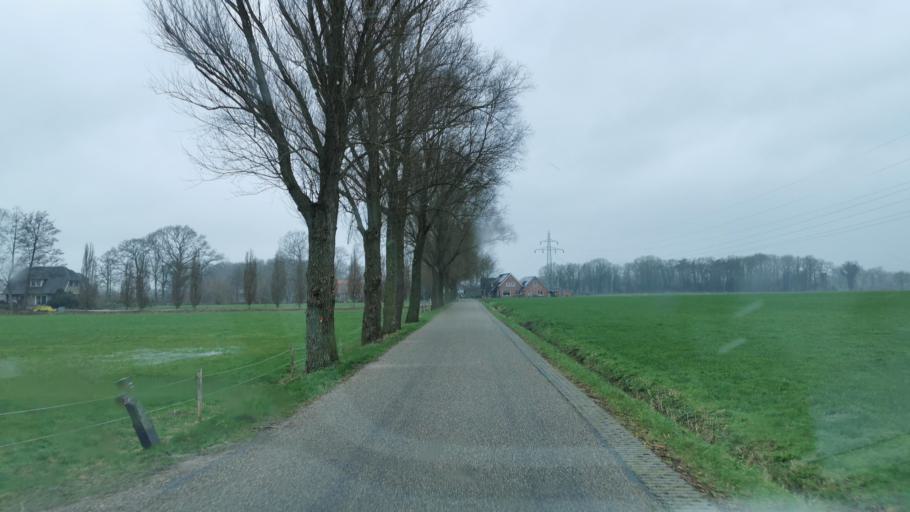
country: NL
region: Overijssel
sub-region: Gemeente Oldenzaal
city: Oldenzaal
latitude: 52.2979
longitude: 6.8623
